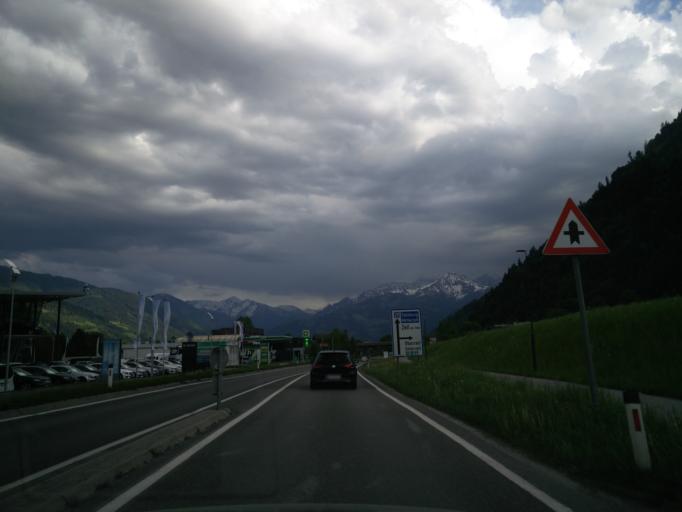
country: AT
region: Salzburg
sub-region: Politischer Bezirk Zell am See
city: Maishofen
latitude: 47.3517
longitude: 12.8001
